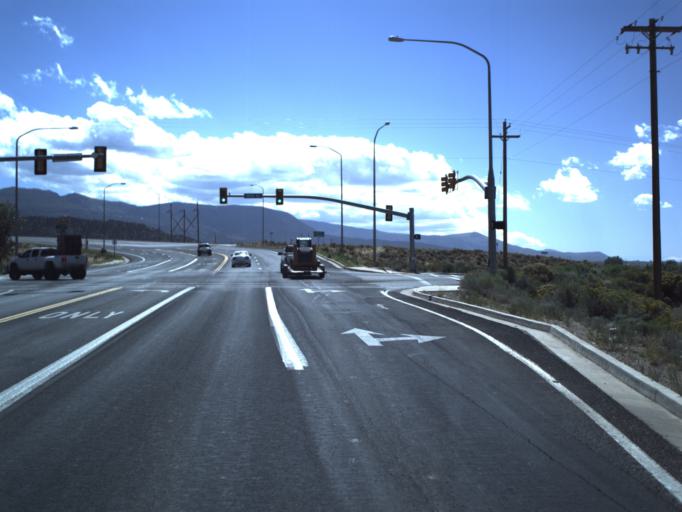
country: US
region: Utah
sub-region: Iron County
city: Enoch
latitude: 37.7319
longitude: -113.0553
